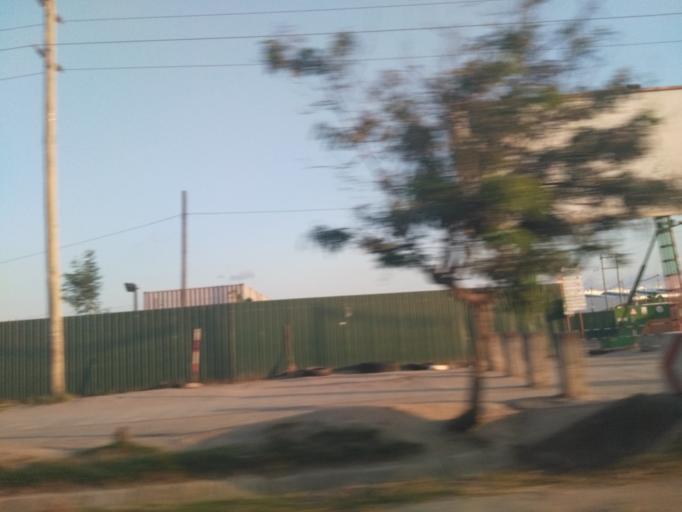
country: TZ
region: Dar es Salaam
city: Dar es Salaam
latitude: -6.8611
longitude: 39.2108
